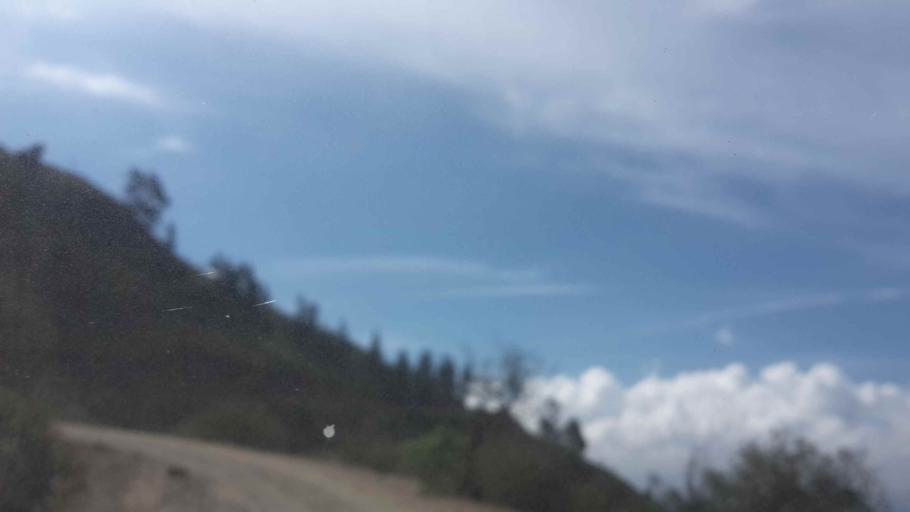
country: BO
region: Cochabamba
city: Cochabamba
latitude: -17.3616
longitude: -66.0580
